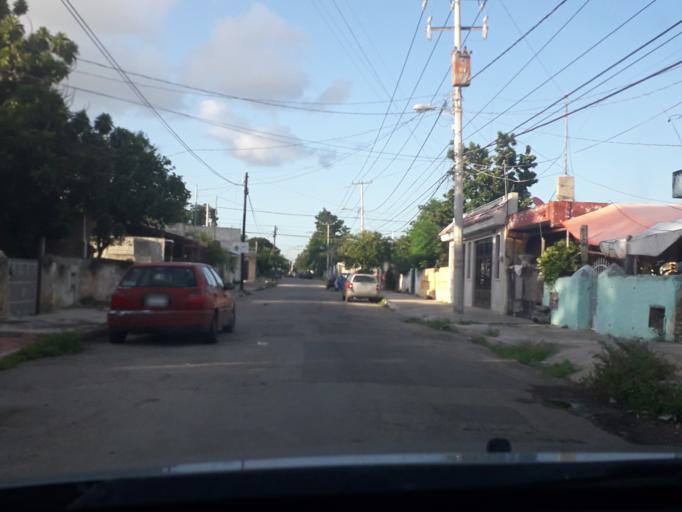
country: MX
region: Yucatan
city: Merida
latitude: 20.9740
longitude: -89.6465
